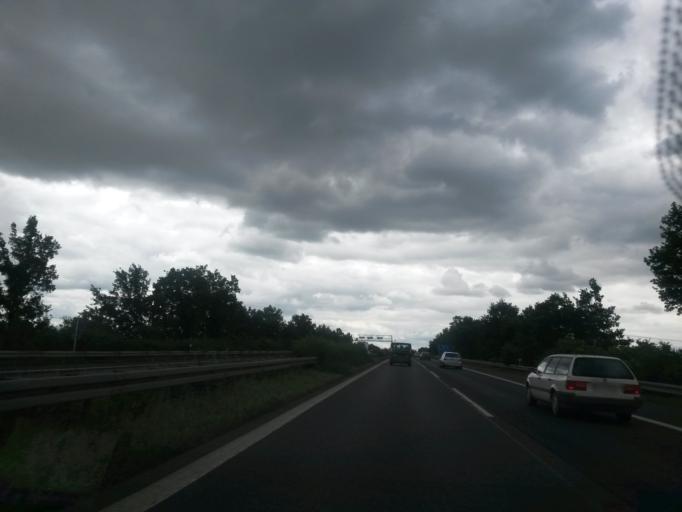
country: DE
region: Bavaria
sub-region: Regierungsbezirk Mittelfranken
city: Furth
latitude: 49.5293
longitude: 10.9923
